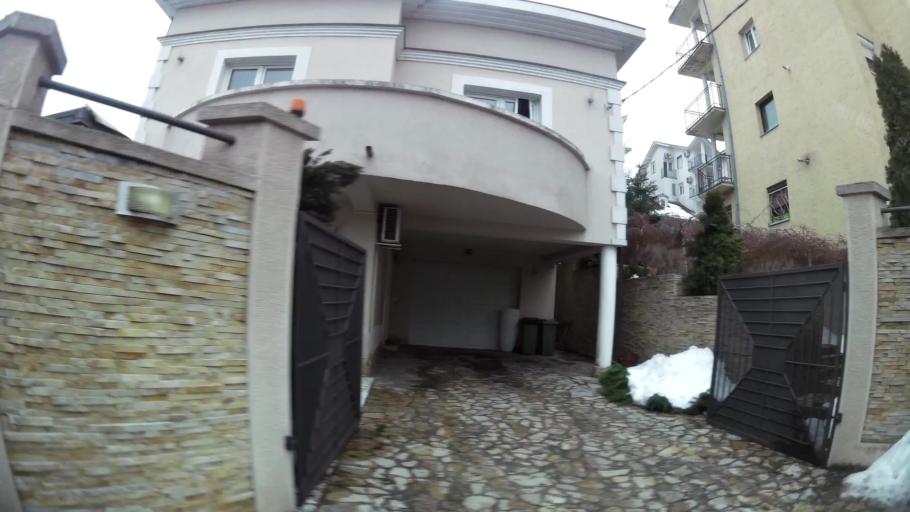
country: RS
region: Central Serbia
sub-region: Belgrade
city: Vozdovac
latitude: 44.7648
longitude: 20.5015
